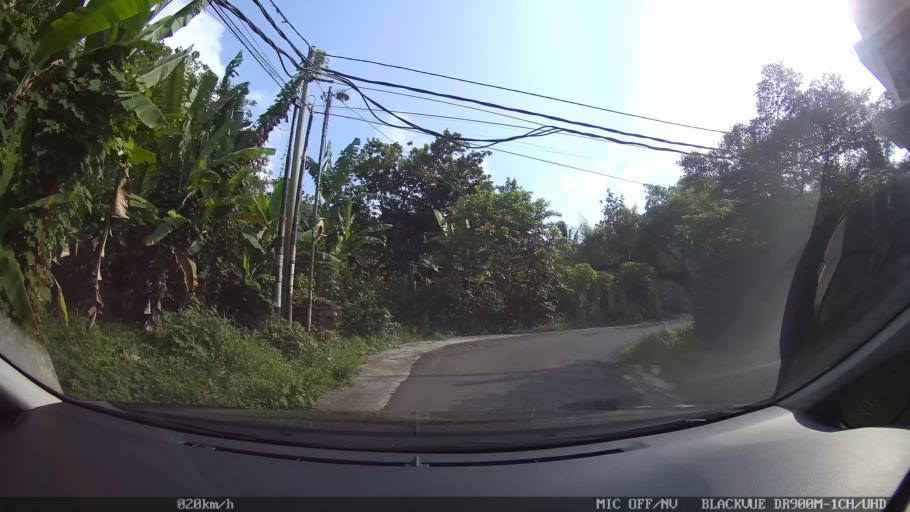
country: ID
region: Lampung
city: Bandarlampung
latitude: -5.4285
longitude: 105.2495
